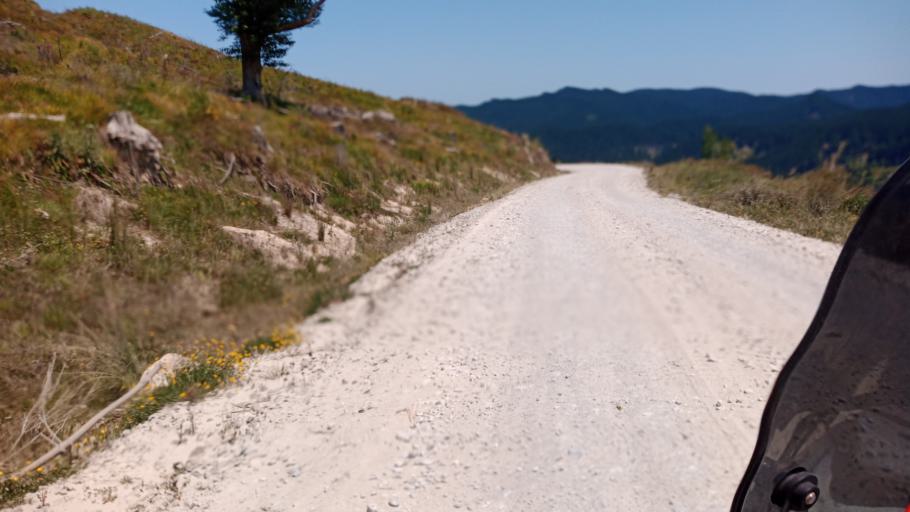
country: NZ
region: Gisborne
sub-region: Gisborne District
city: Gisborne
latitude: -38.2901
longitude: 178.0102
